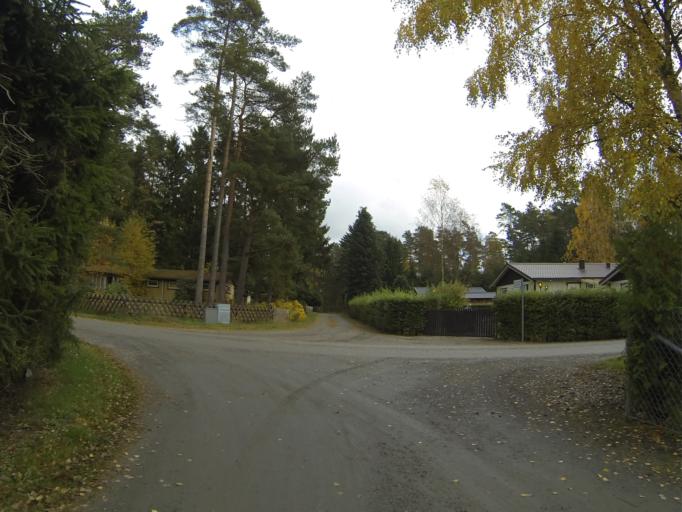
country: SE
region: Skane
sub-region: Sjobo Kommun
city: Sjoebo
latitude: 55.6321
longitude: 13.6526
